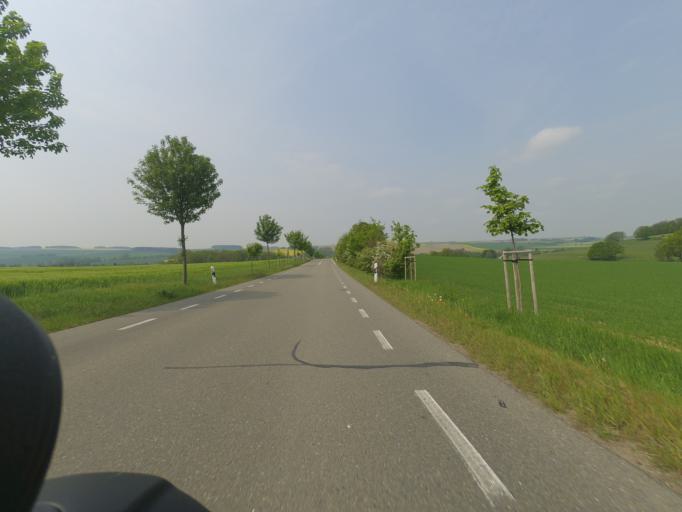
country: DE
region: Saxony
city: Pretzschendorf
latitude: 50.8590
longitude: 13.4796
